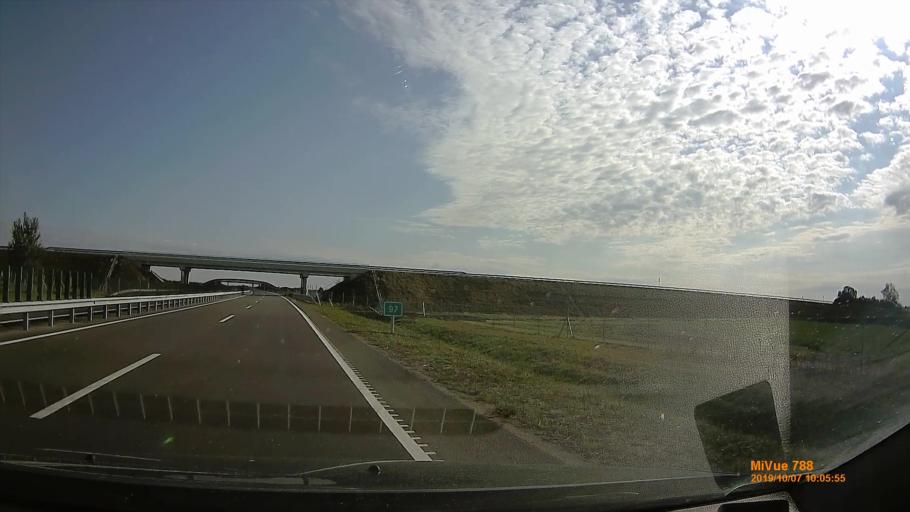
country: HU
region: Bekes
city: Kondoros
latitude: 46.7378
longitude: 20.8066
